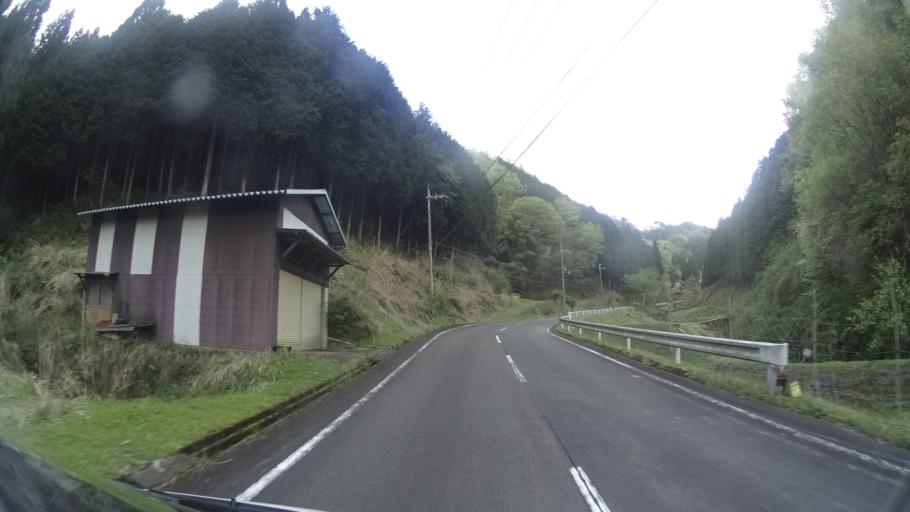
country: JP
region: Kyoto
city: Ayabe
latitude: 35.2556
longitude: 135.3142
